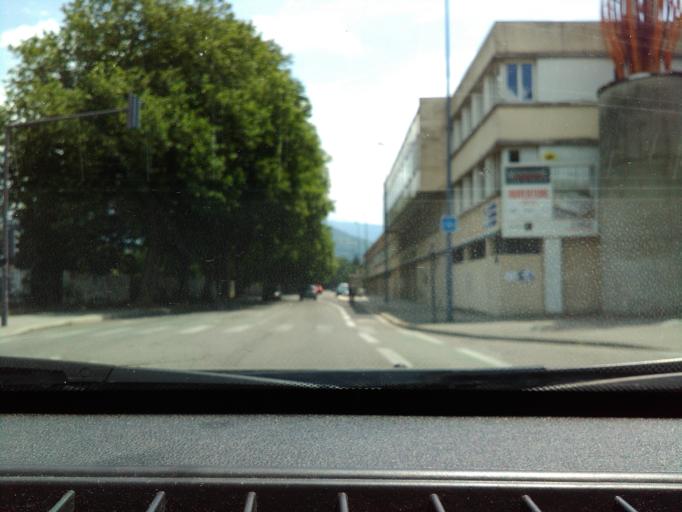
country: FR
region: Rhone-Alpes
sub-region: Departement de l'Isere
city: Grenoble
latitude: 45.1706
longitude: 5.7274
